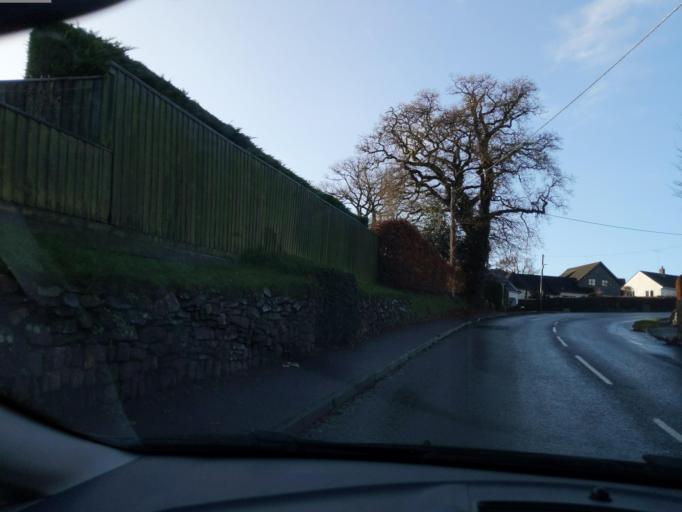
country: GB
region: England
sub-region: Devon
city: Okehampton
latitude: 50.7406
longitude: -4.0070
